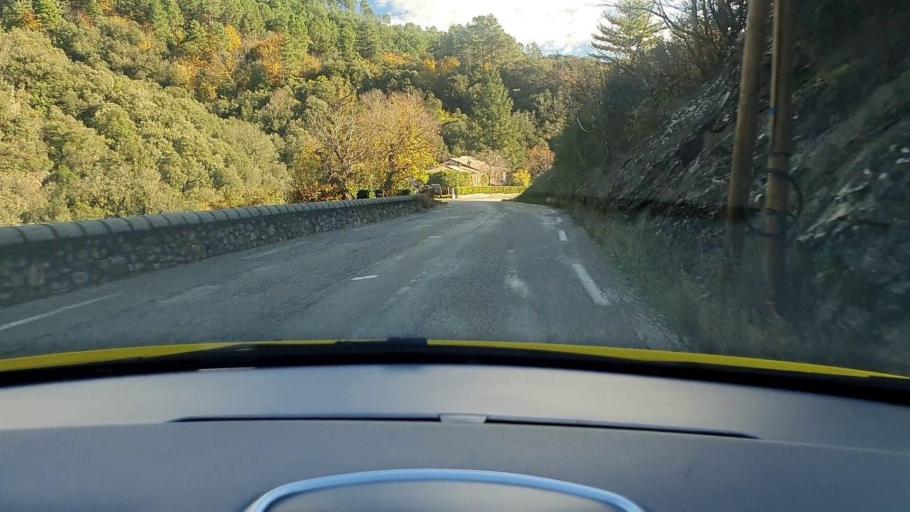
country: FR
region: Languedoc-Roussillon
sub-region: Departement du Gard
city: Valleraugue
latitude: 44.1275
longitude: 3.7407
